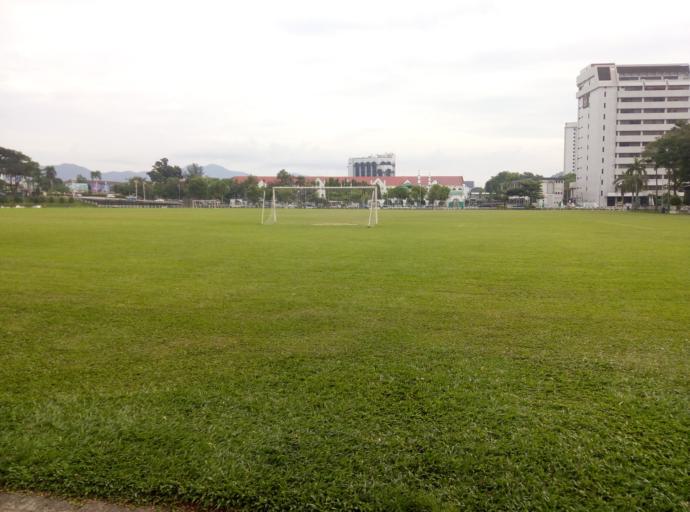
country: MY
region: Perak
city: Ipoh
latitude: 4.5979
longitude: 101.0772
